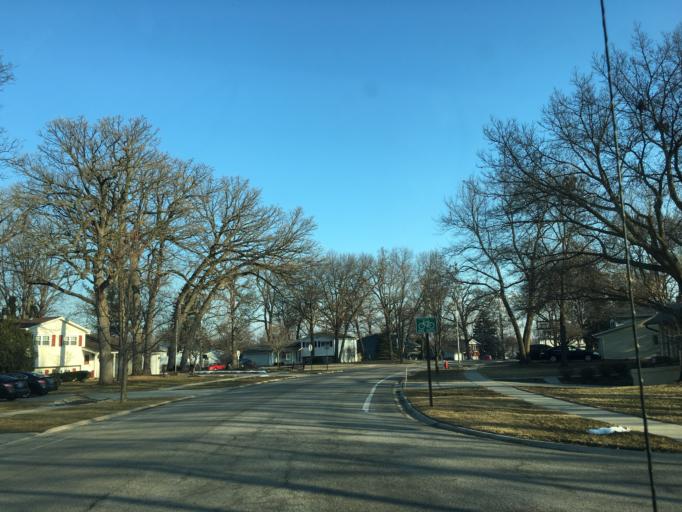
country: US
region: Illinois
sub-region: Cook County
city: Schaumburg
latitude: 42.0249
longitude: -88.0914
